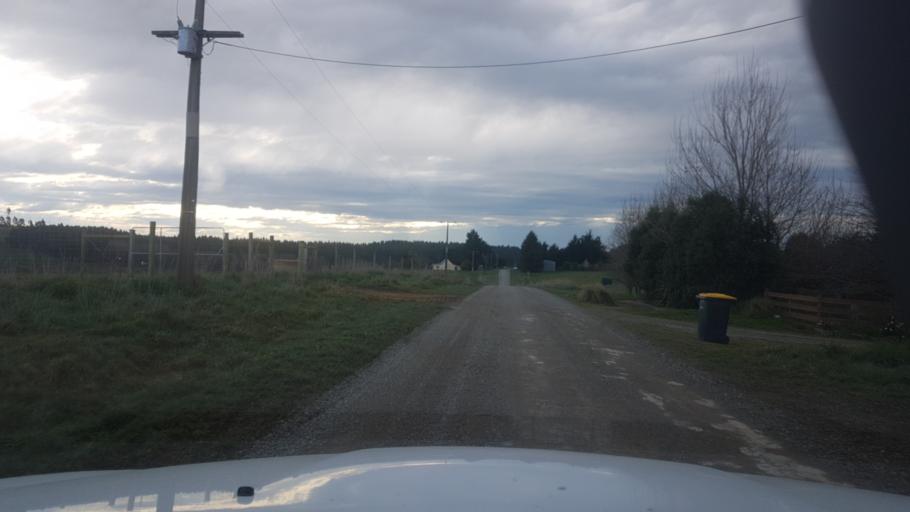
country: NZ
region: Canterbury
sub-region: Timaru District
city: Pleasant Point
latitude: -44.3346
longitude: 171.1532
